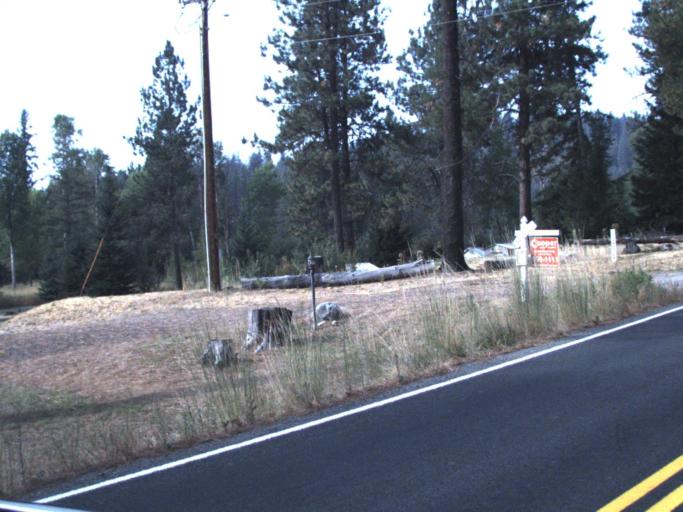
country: US
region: Washington
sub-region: Spokane County
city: Trentwood
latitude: 47.8229
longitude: -117.2112
